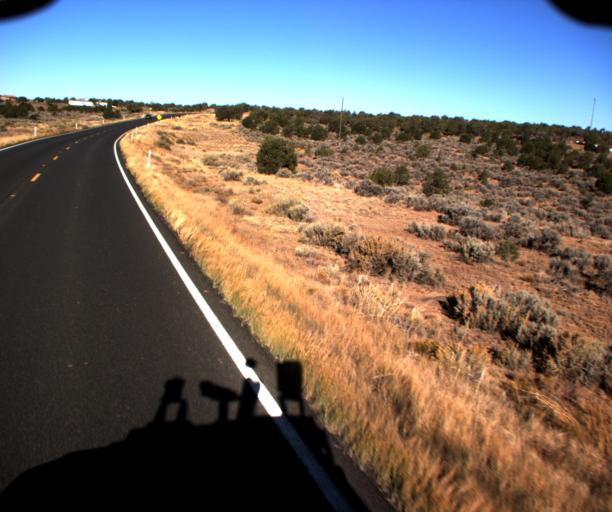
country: US
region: Arizona
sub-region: Apache County
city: Ganado
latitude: 35.7617
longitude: -109.7823
